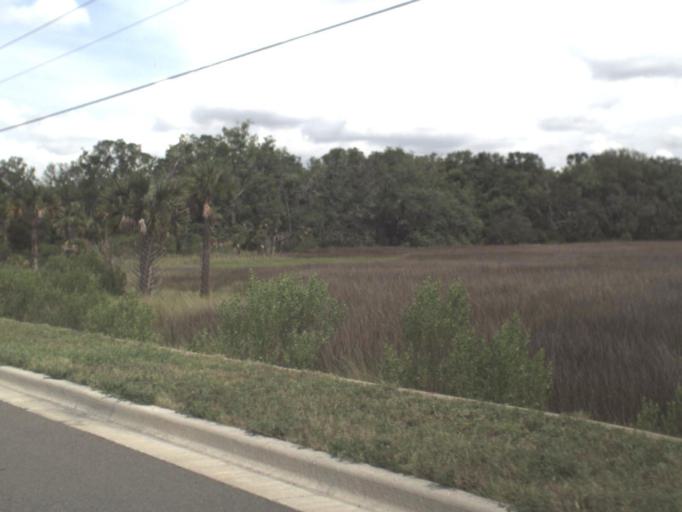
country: US
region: Florida
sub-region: Duval County
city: Jacksonville
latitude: 30.4144
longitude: -81.5904
